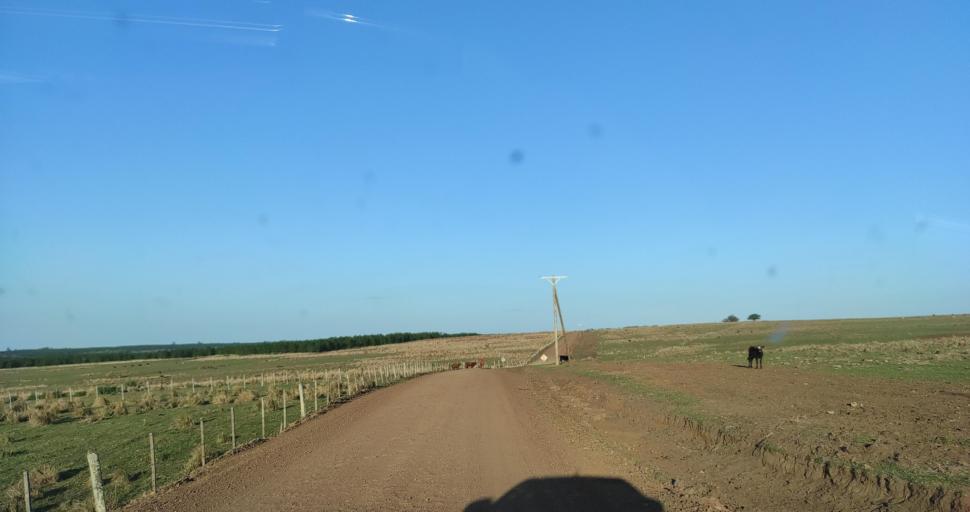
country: PY
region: Itapua
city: Carmen del Parana
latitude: -27.4124
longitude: -56.1430
